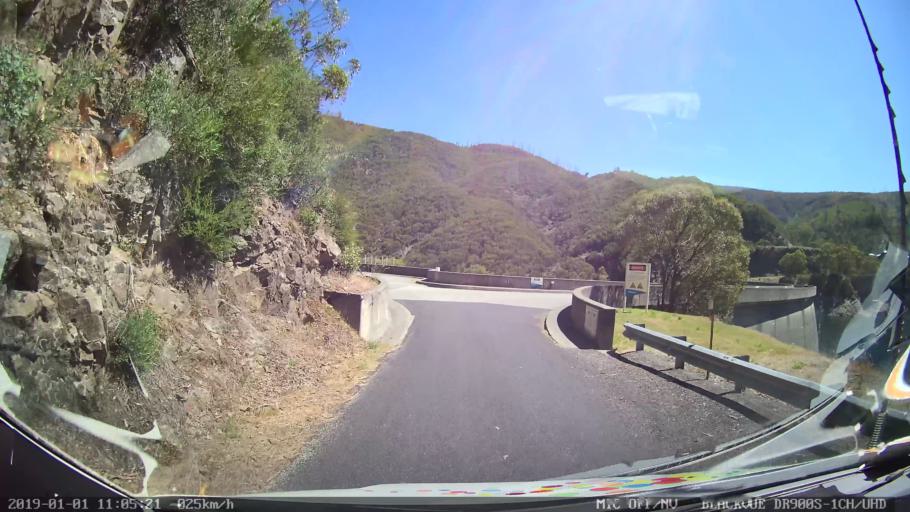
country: AU
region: New South Wales
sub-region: Snowy River
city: Jindabyne
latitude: -35.9660
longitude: 148.3894
